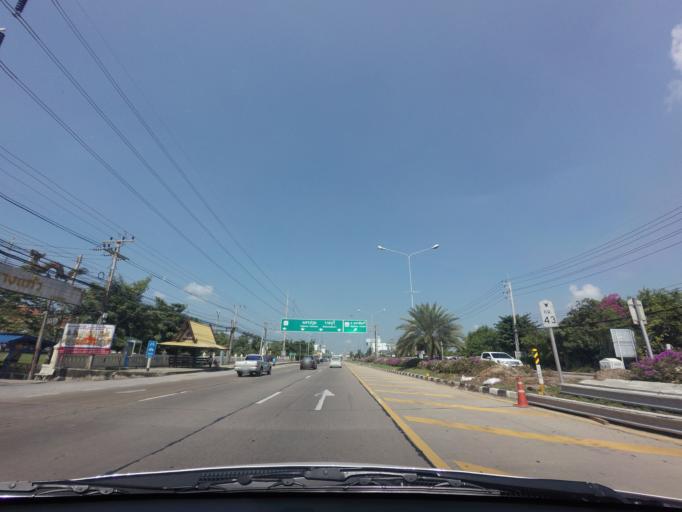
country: TH
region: Nakhon Pathom
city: Nakhon Chai Si
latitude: 13.7882
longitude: 100.1722
